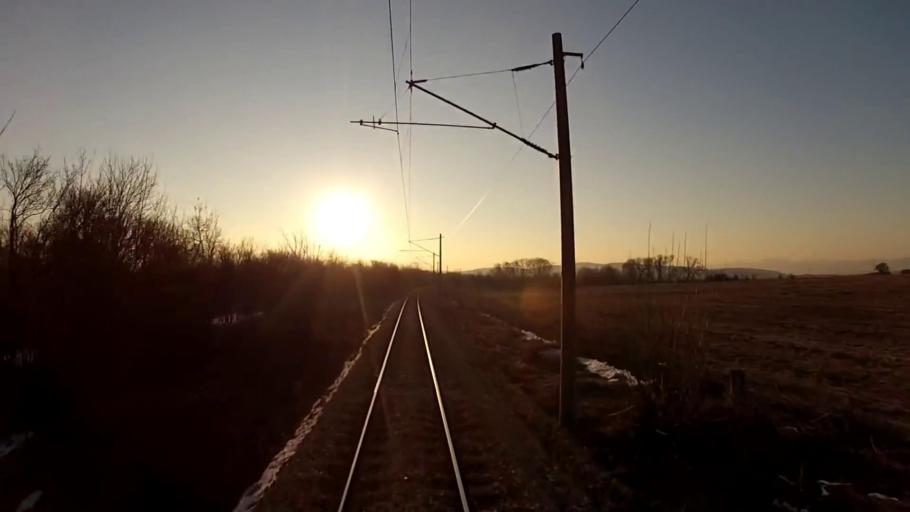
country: BG
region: Sofiya
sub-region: Obshtina Dragoman
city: Dragoman
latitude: 42.8855
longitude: 22.9797
